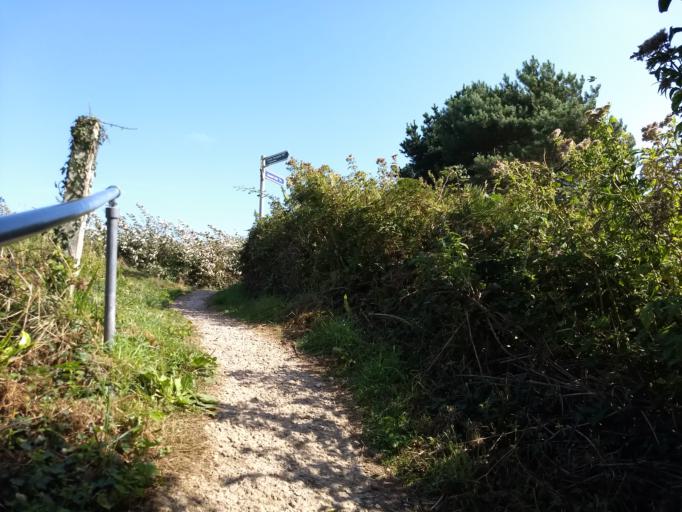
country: GB
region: England
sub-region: Isle of Wight
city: Totland
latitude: 50.6899
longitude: -1.5371
